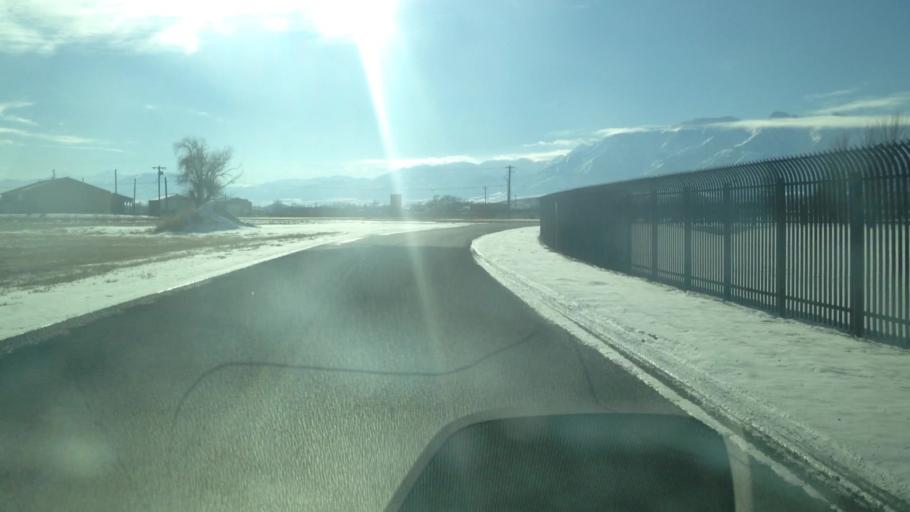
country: US
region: Utah
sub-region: Cache County
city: Logan
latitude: 41.7372
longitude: -111.8641
